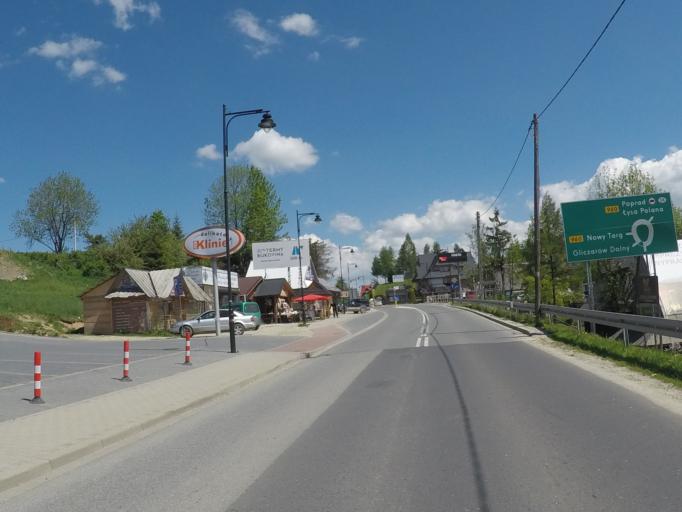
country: PL
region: Lesser Poland Voivodeship
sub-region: Powiat tatrzanski
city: Bukowina Tatrzanska
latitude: 49.3296
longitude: 20.0951
